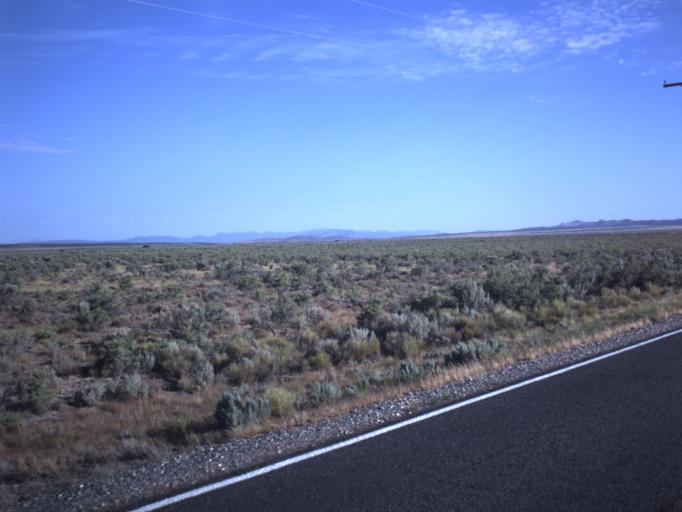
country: US
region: Utah
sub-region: Iron County
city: Enoch
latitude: 37.8214
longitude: -113.0504
